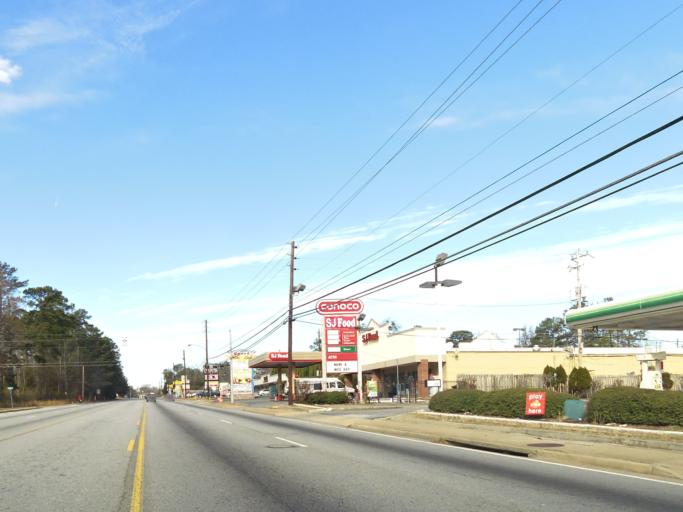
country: US
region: Georgia
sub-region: Bibb County
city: Macon
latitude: 32.8221
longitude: -83.6982
